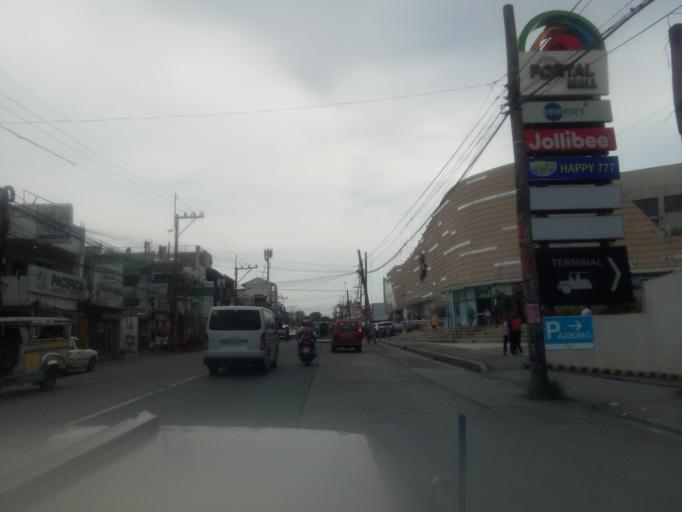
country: PH
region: Calabarzon
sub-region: Province of Cavite
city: Bulihan
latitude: 14.2950
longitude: 121.0069
